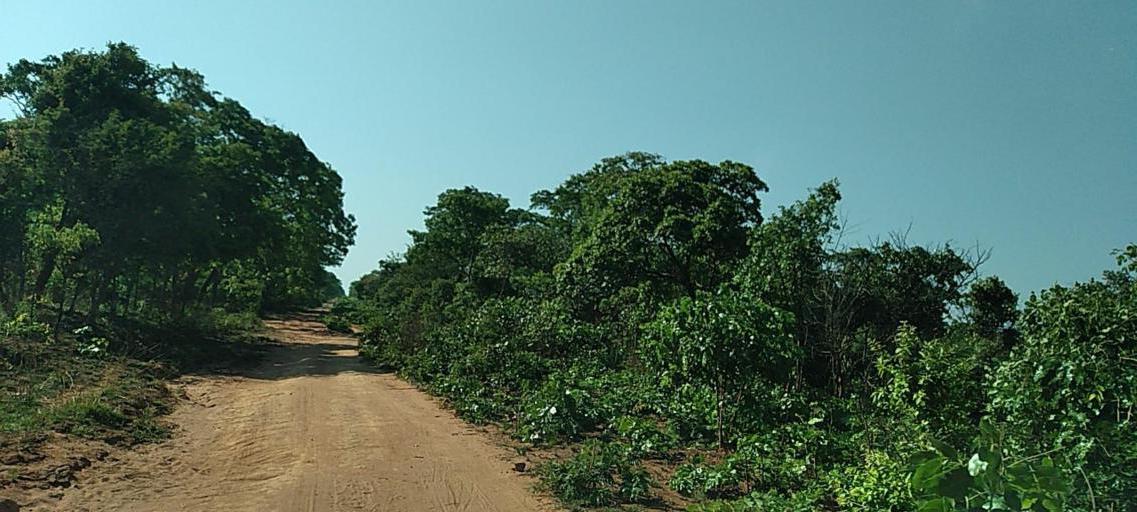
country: ZM
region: Central
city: Mkushi
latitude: -13.4715
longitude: 28.9178
